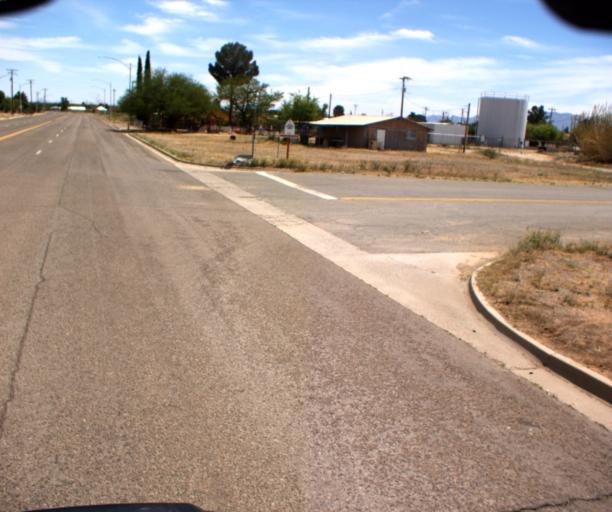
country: US
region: Arizona
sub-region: Cochise County
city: Willcox
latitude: 32.3262
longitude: -109.4873
